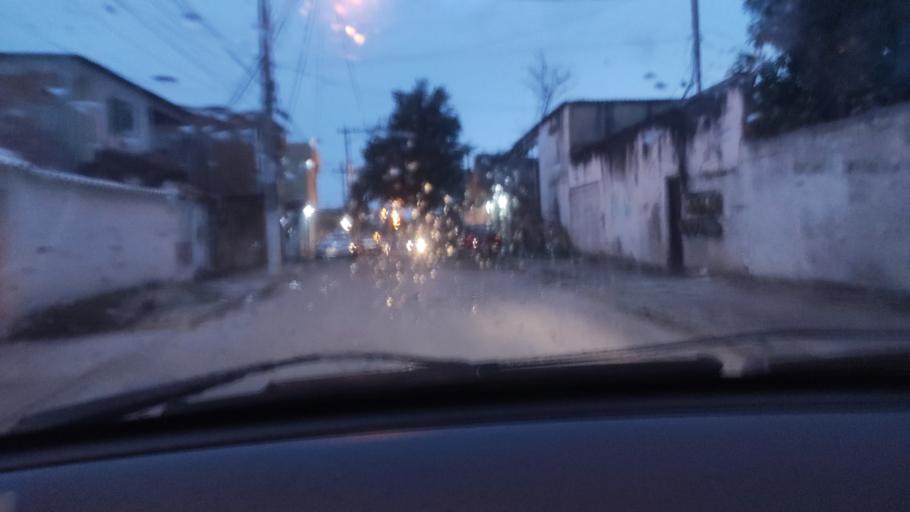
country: BR
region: Rio de Janeiro
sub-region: Itaborai
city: Itaborai
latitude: -22.7787
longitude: -42.9407
